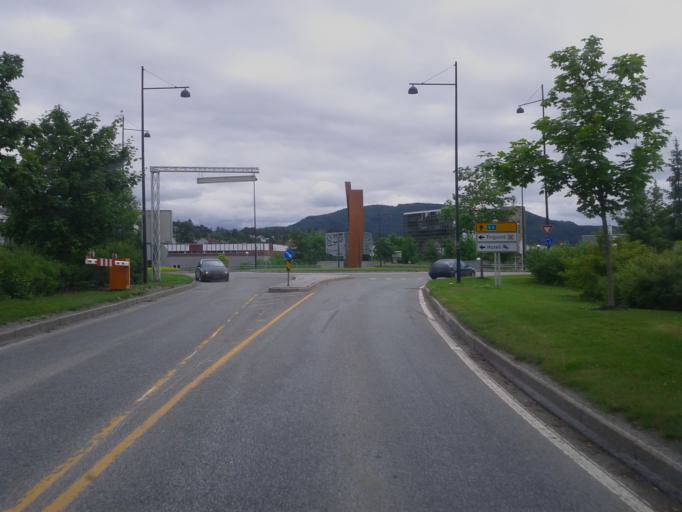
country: NO
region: Nord-Trondelag
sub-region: Steinkjer
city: Steinkjer
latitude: 64.0216
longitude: 11.4900
